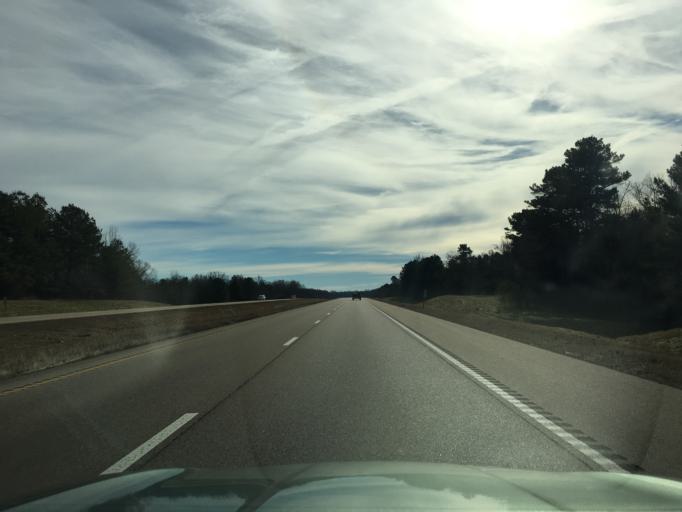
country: US
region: Mississippi
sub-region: Marshall County
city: Holly Springs
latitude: 34.7057
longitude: -89.4021
